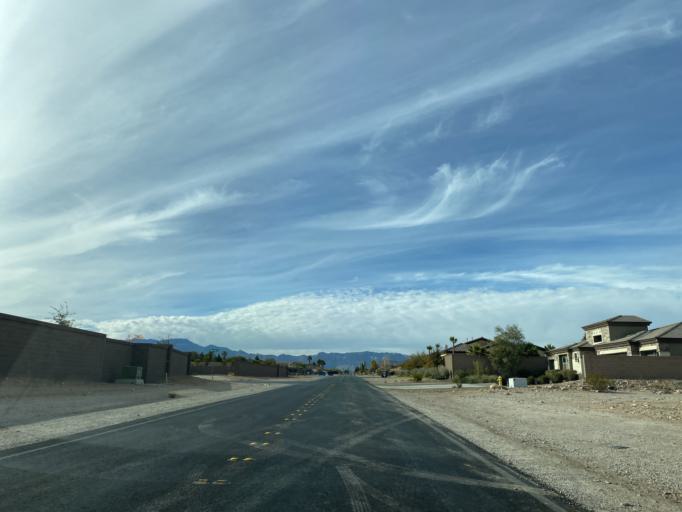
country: US
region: Nevada
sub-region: Clark County
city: Enterprise
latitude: 36.0338
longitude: -115.2570
